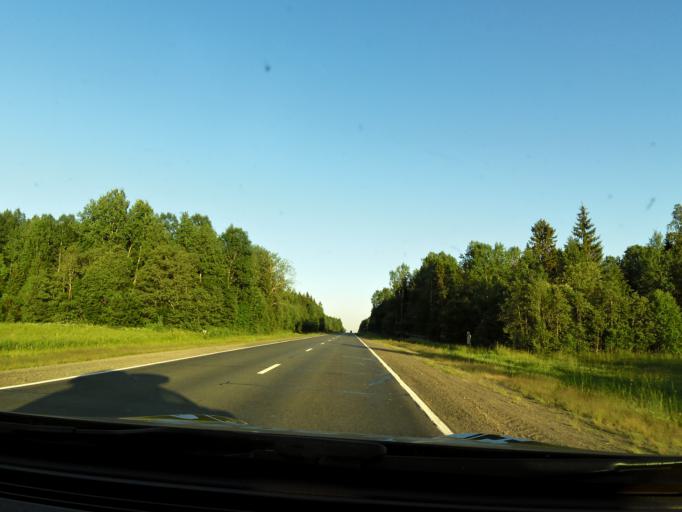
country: RU
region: Vologda
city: Gryazovets
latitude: 58.8130
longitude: 40.2370
